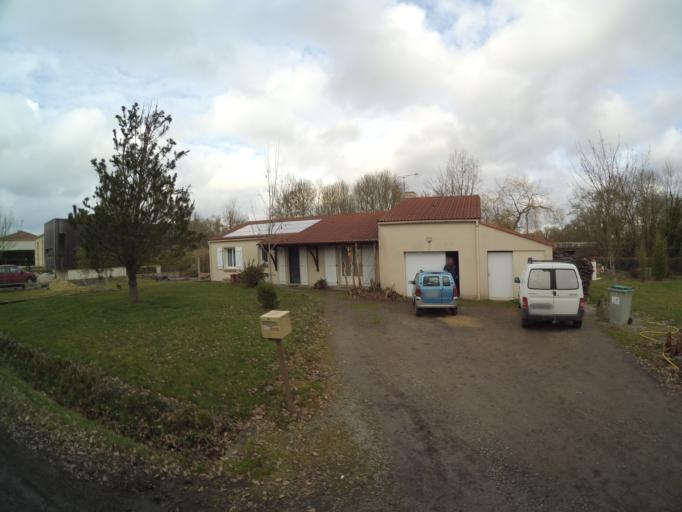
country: FR
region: Pays de la Loire
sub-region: Departement de la Vendee
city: La Bernardiere
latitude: 47.0471
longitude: -1.2850
